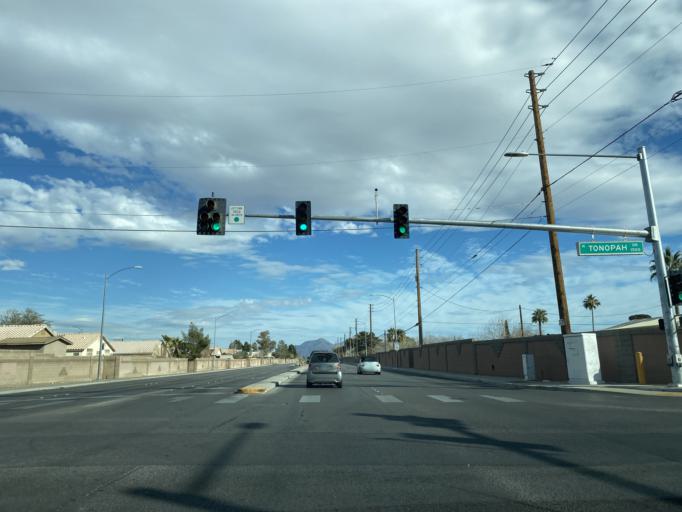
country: US
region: Nevada
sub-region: Clark County
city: Las Vegas
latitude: 36.1884
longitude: -115.1699
